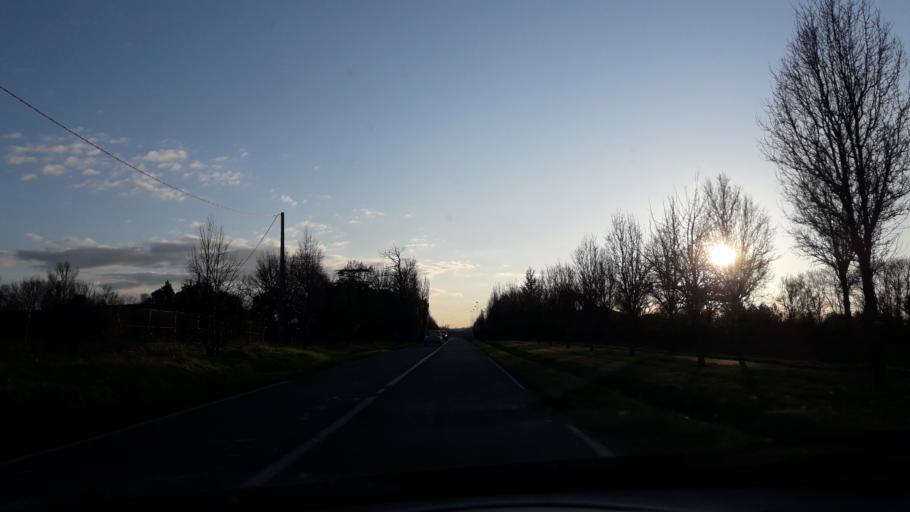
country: FR
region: Midi-Pyrenees
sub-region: Departement de la Haute-Garonne
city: Levignac
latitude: 43.6455
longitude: 1.1642
